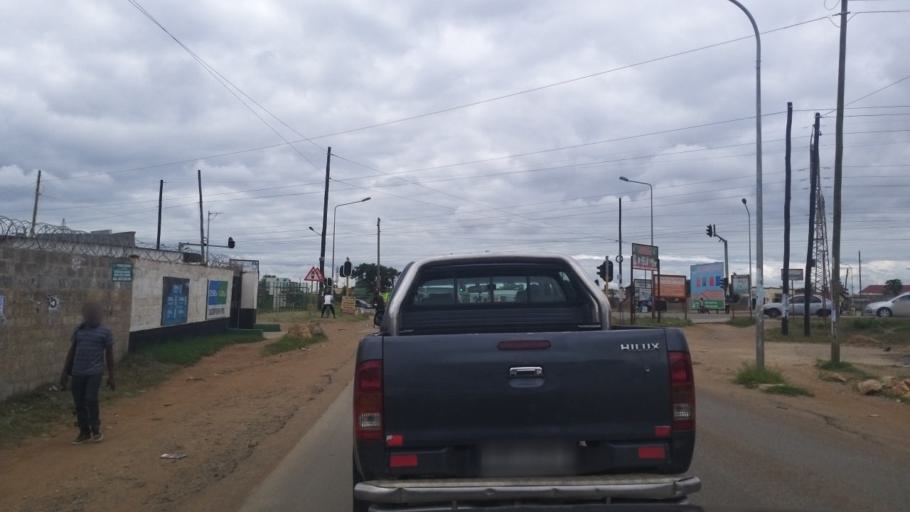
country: ZM
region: Lusaka
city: Lusaka
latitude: -15.4462
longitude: 28.3053
